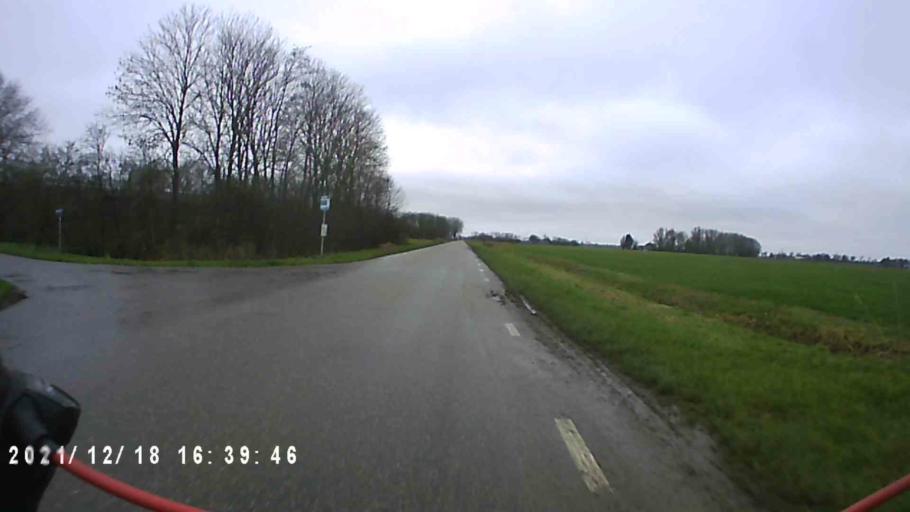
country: NL
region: Friesland
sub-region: Gemeente Dongeradeel
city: Dokkum
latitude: 53.3604
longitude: 6.0053
